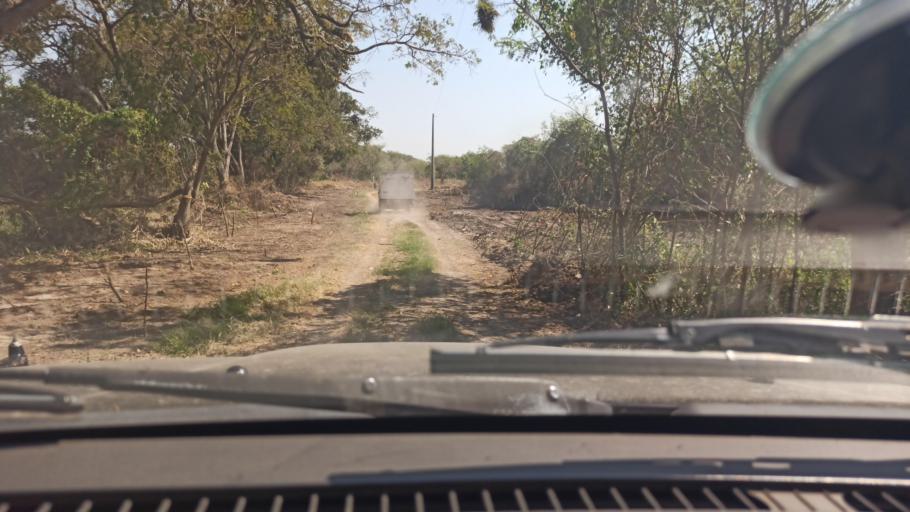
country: PY
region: Asuncion
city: Asuncion
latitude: -25.3457
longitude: -57.6743
